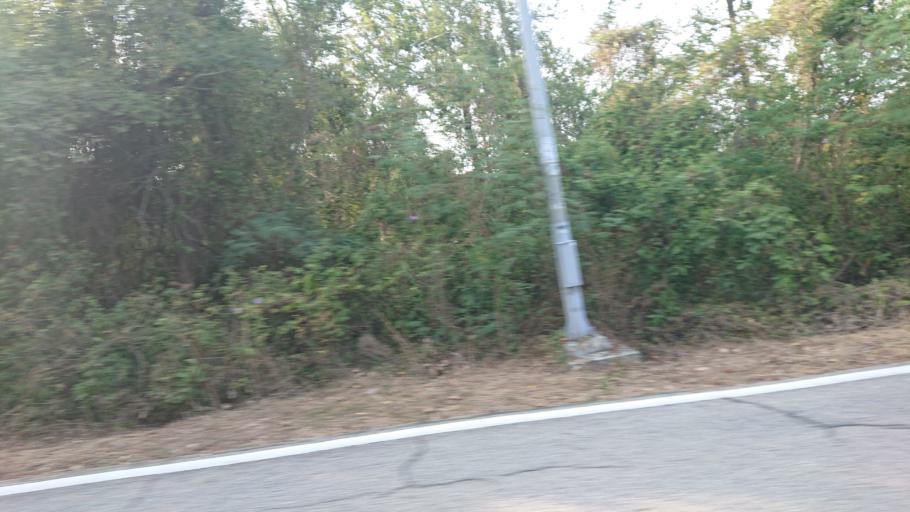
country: CN
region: Fujian
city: Shijing
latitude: 24.5009
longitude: 118.4427
